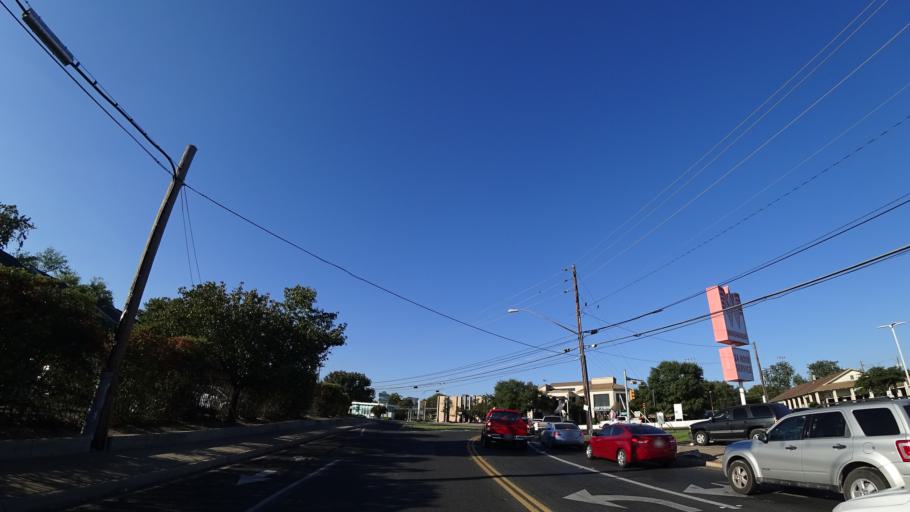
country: US
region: Texas
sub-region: Travis County
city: Austin
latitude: 30.2310
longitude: -97.7359
